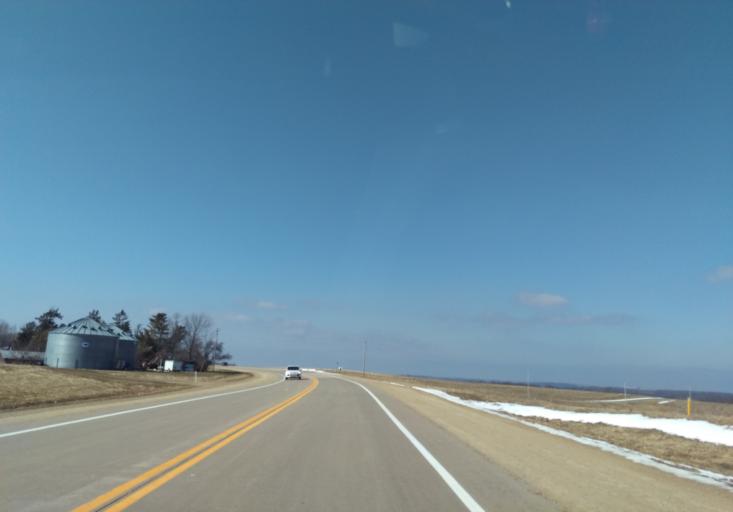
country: US
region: Wisconsin
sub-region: La Crosse County
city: La Crosse
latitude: 43.7309
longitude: -91.0924
